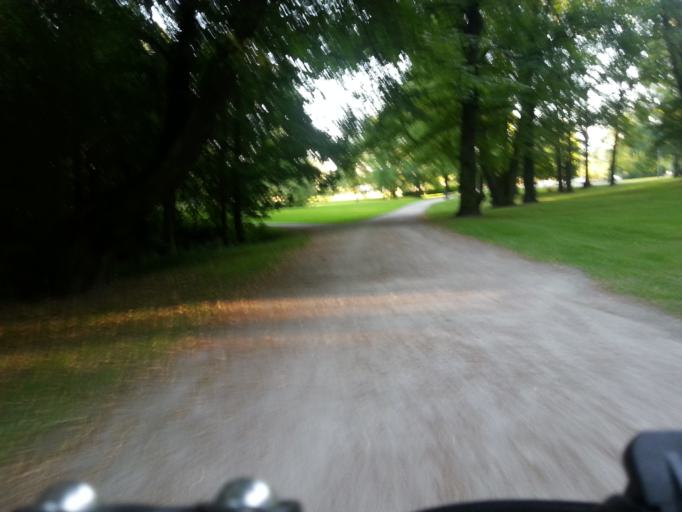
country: FI
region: Uusimaa
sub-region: Helsinki
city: Helsinki
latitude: 60.1866
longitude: 24.9347
